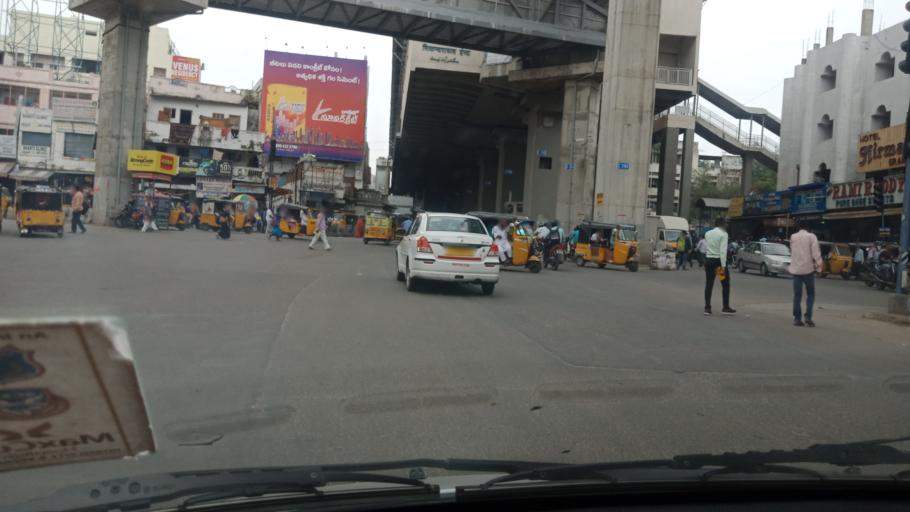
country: IN
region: Telangana
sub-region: Hyderabad
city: Malkajgiri
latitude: 17.4347
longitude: 78.5056
